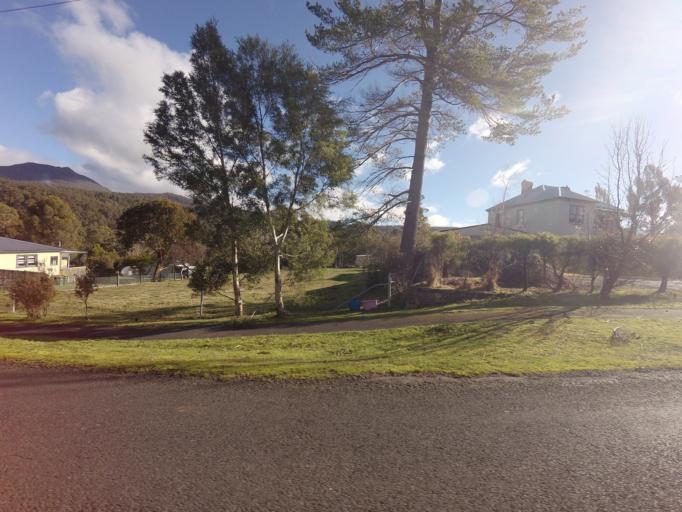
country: AU
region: Tasmania
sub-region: Glenorchy
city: Berriedale
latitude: -42.8409
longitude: 147.1959
